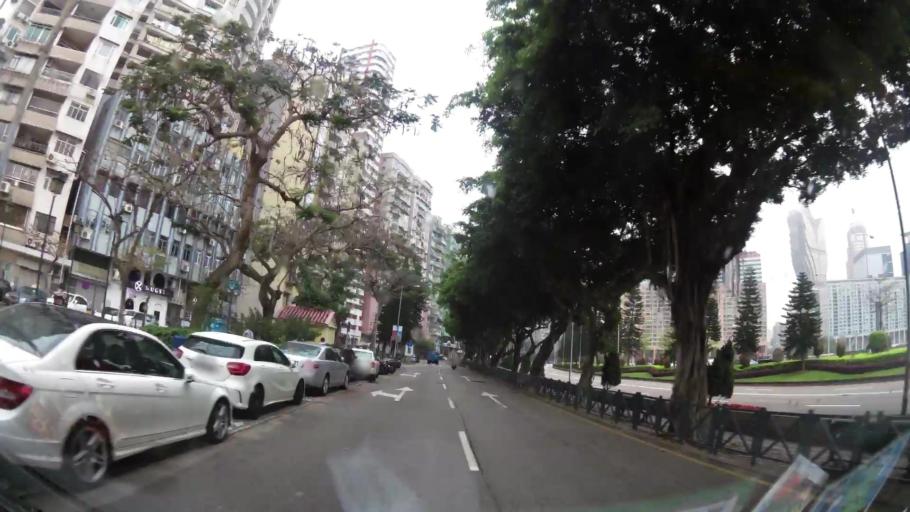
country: MO
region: Macau
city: Macau
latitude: 22.1876
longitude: 113.5376
